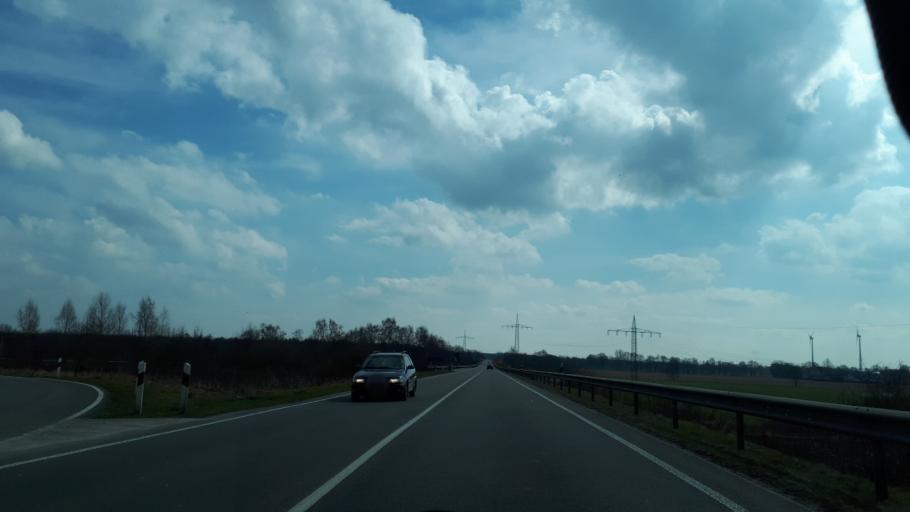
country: DE
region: Lower Saxony
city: Vechta
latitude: 52.7281
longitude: 8.2523
